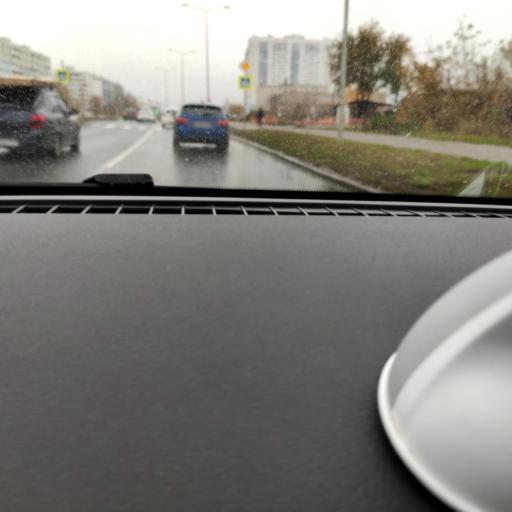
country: RU
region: Samara
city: Samara
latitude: 53.2623
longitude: 50.2375
